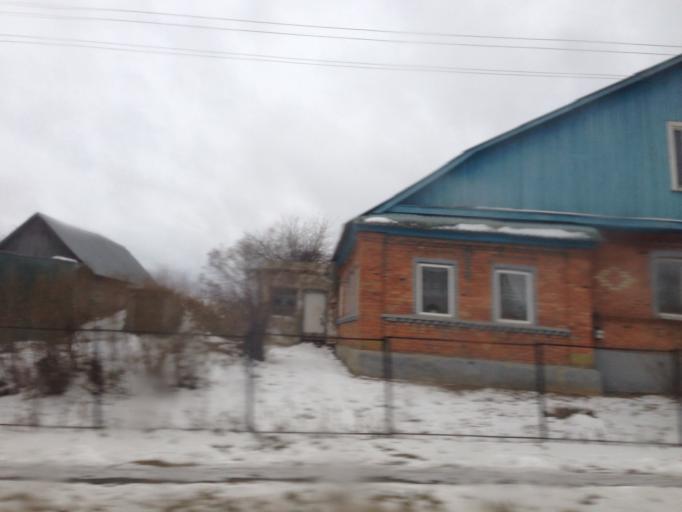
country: RU
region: Tula
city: Skuratovskiy
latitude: 54.1345
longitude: 37.6783
